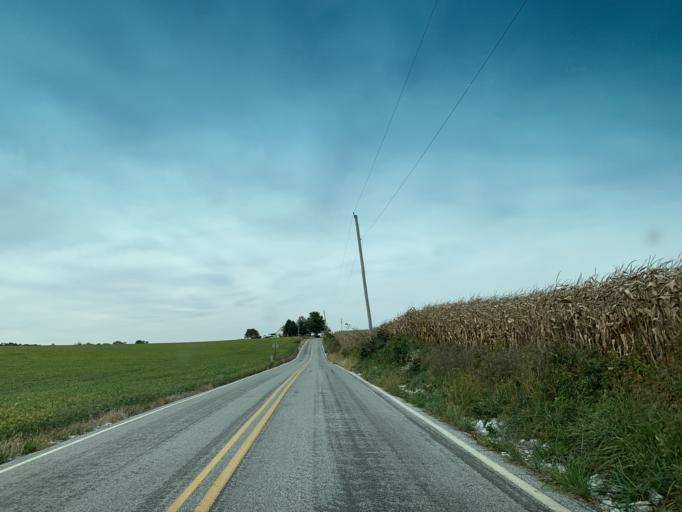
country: US
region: Pennsylvania
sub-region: York County
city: Stewartstown
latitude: 39.8052
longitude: -76.5197
